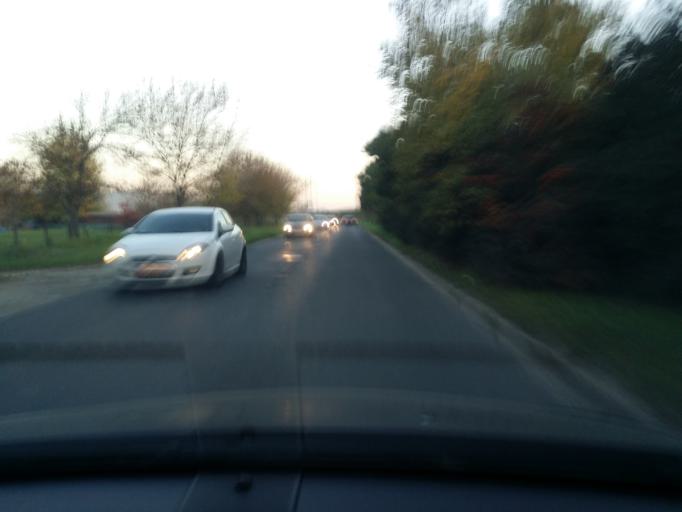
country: HU
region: Budapest
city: Budapest XV. keruelet
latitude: 47.5838
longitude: 19.1346
